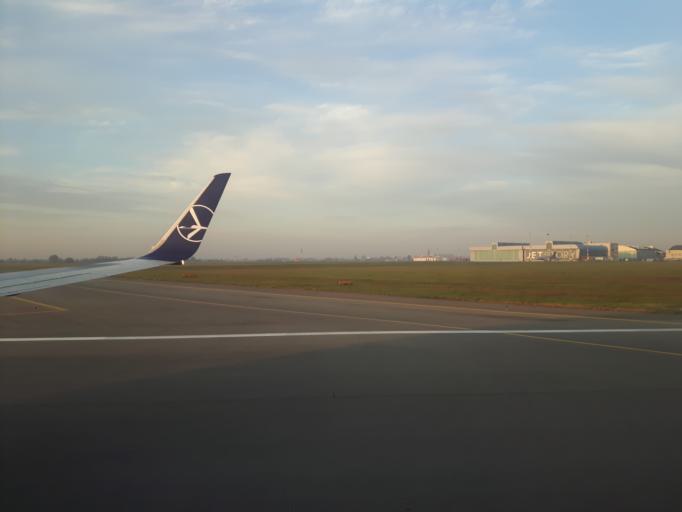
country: PL
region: Masovian Voivodeship
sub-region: Warszawa
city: Wlochy
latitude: 52.1757
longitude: 20.9599
